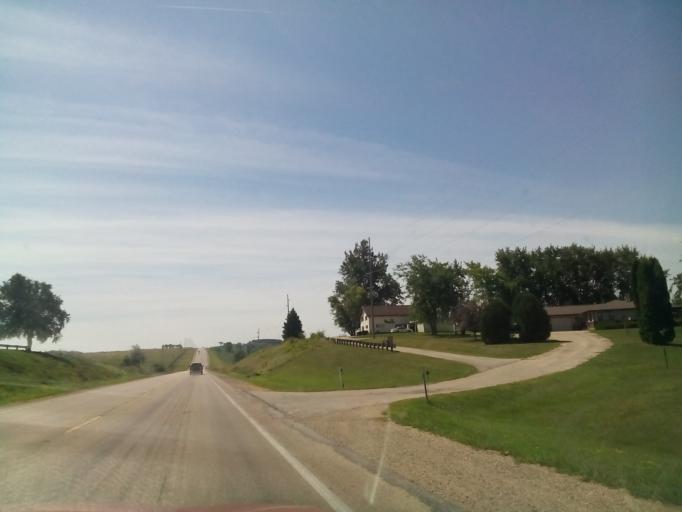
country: US
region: Wisconsin
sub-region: Green County
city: Monticello
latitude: 42.6988
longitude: -89.6169
